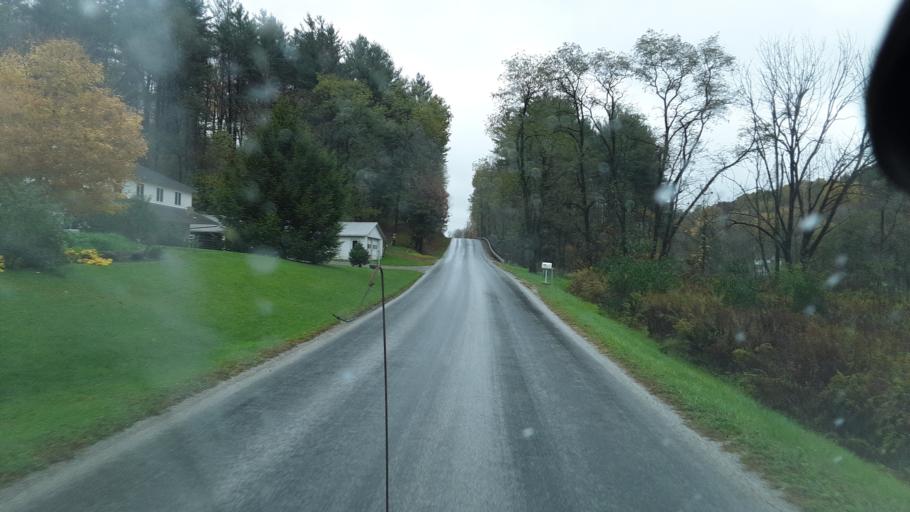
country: US
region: Ohio
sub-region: Coshocton County
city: West Lafayette
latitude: 40.3938
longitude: -81.7626
